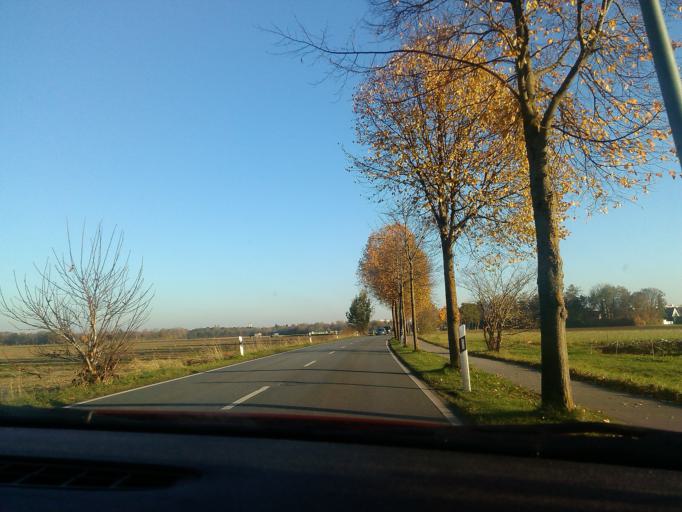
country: DE
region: Bavaria
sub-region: Upper Bavaria
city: Pasing
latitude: 48.1350
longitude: 11.4645
